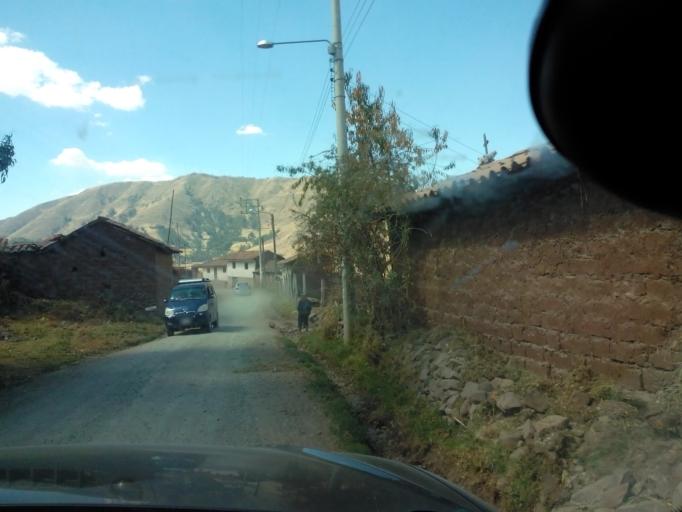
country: PE
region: Cusco
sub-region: Provincia de Anta
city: Huarocondo
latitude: -13.4362
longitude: -72.2268
